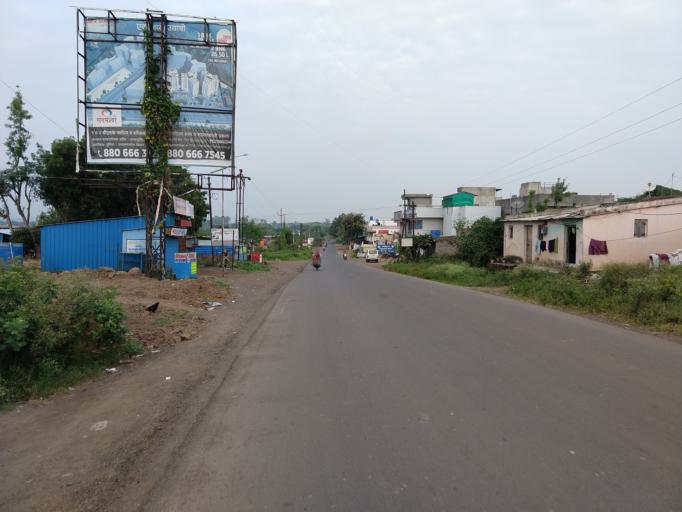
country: IN
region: Maharashtra
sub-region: Pune Division
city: Sasvad
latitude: 18.3468
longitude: 74.0256
